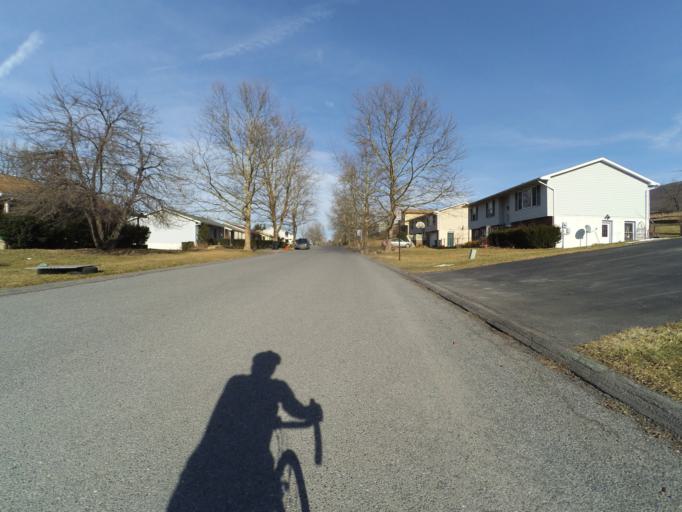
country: US
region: Pennsylvania
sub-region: Centre County
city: Lemont
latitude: 40.8187
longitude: -77.8130
